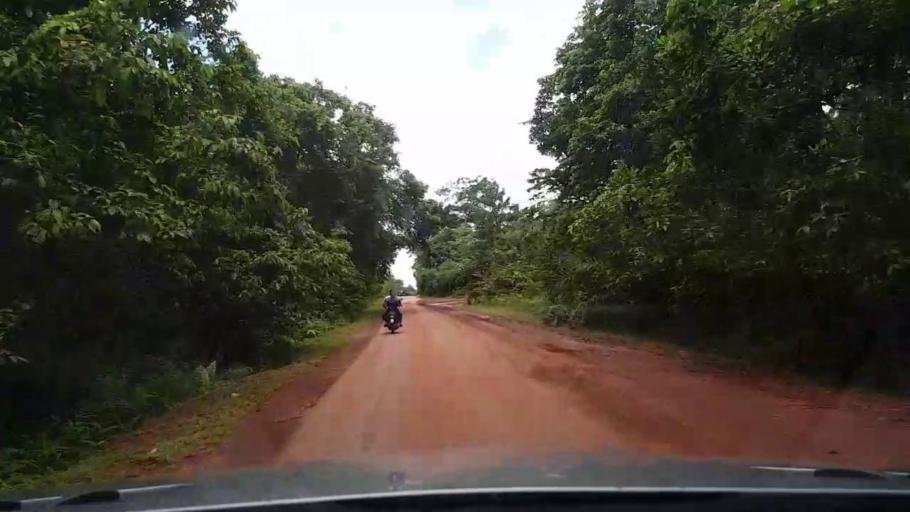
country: MY
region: Pahang
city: Pekan
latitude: 3.1345
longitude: 102.9739
